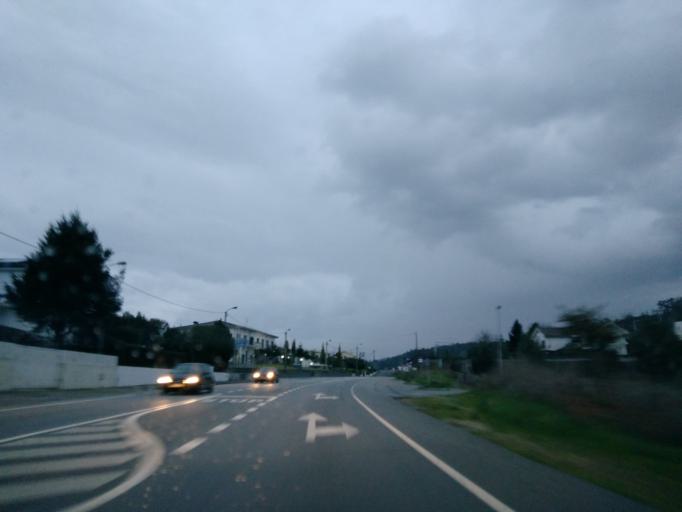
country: PT
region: Braga
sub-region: Braga
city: Oliveira
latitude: 41.4913
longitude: -8.4689
